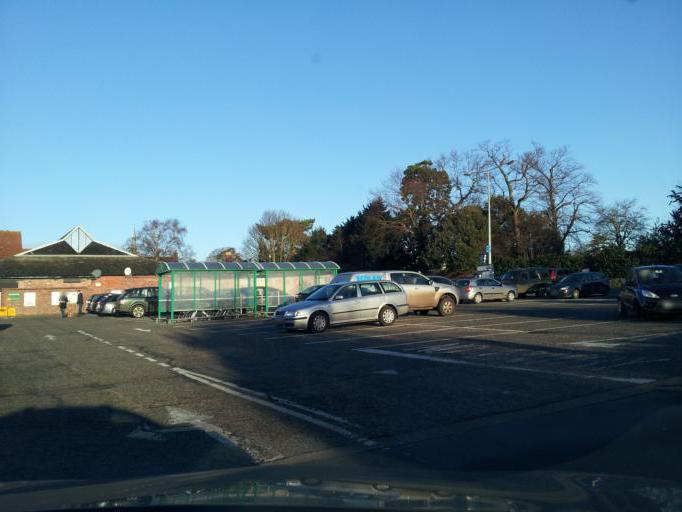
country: GB
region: England
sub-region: Suffolk
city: Woodbridge
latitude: 52.0926
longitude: 1.3211
